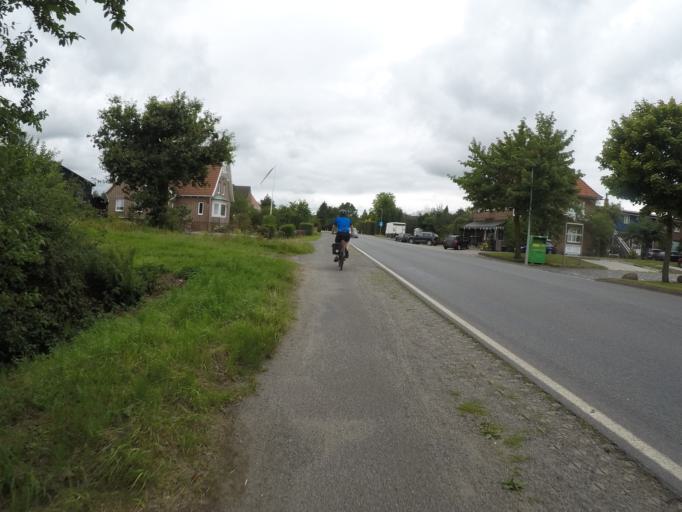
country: DE
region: Schleswig-Holstein
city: Haseldorf
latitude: 53.5889
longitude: 9.5737
